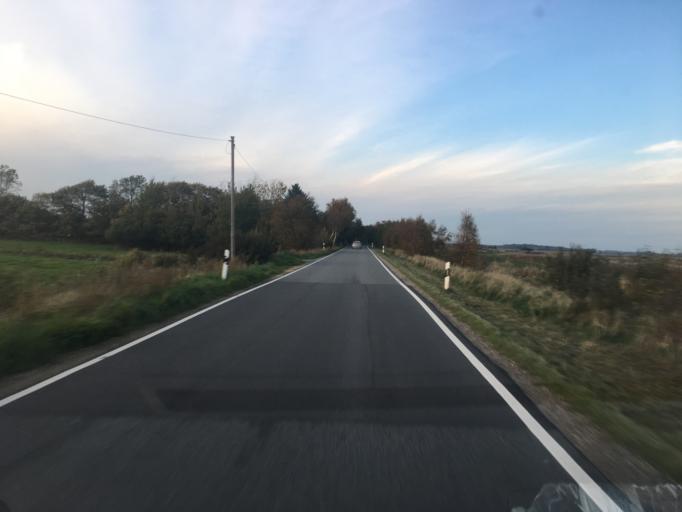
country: DE
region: Schleswig-Holstein
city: Humptrup
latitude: 54.8922
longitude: 8.8484
